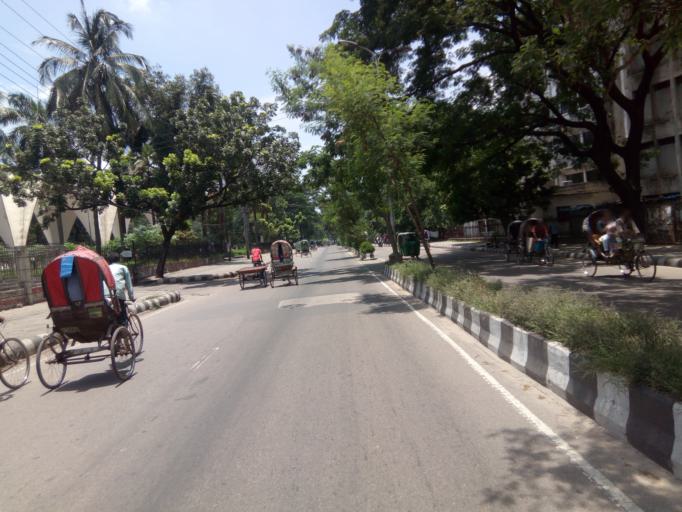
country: BD
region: Dhaka
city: Azimpur
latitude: 23.7294
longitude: 90.3989
